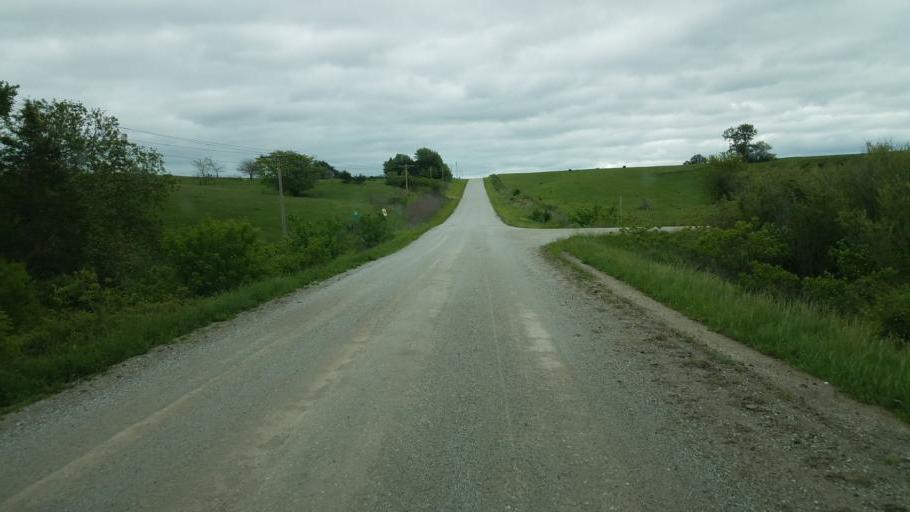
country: US
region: Iowa
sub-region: Decatur County
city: Lamoni
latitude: 40.6382
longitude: -93.8964
